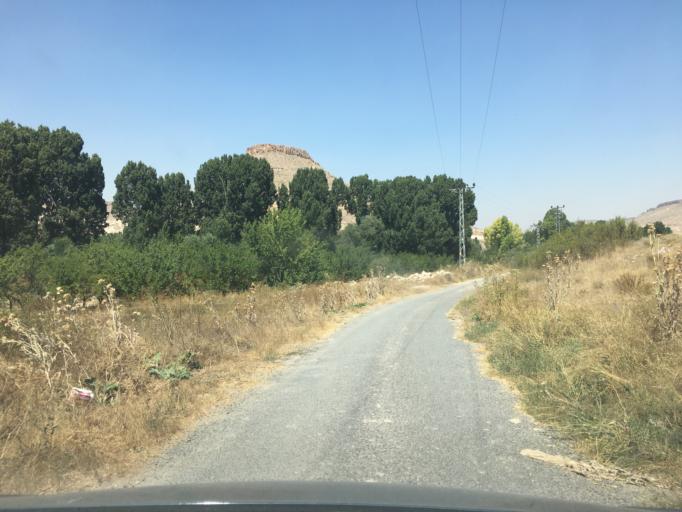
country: TR
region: Kayseri
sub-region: Yesilhisar
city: Yesilhisar
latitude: 38.4662
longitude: 34.9643
